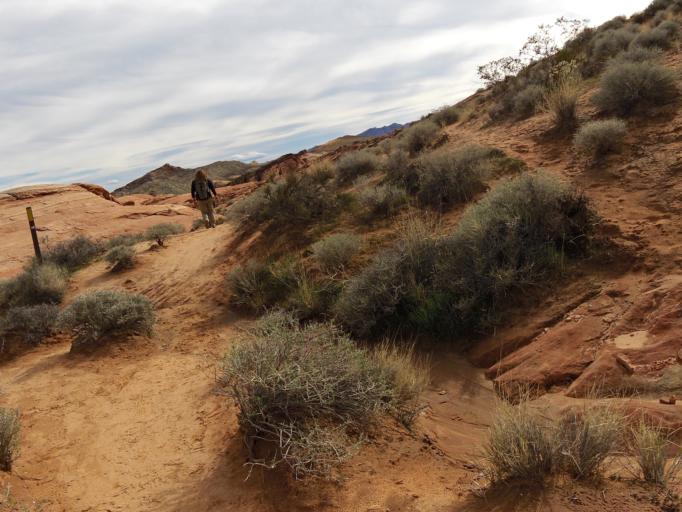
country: US
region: Nevada
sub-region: Clark County
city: Moapa Valley
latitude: 36.4863
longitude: -114.5240
